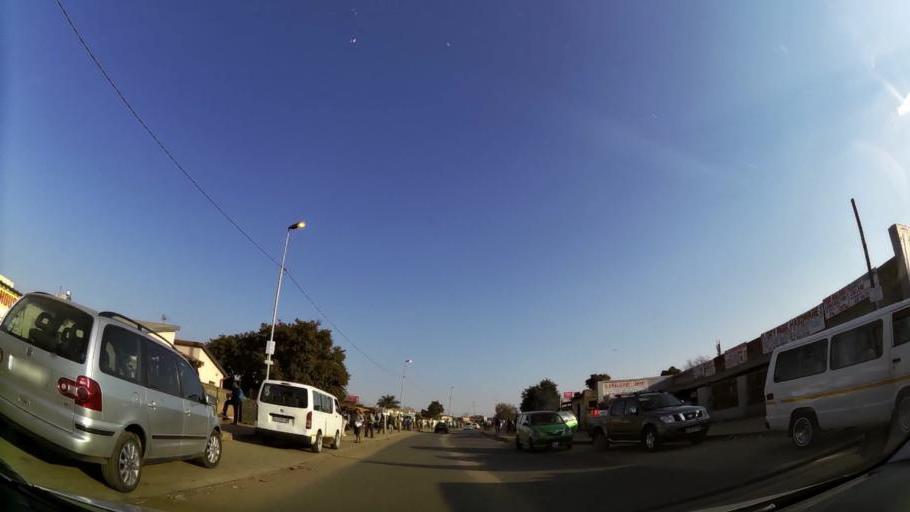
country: ZA
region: Gauteng
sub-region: Ekurhuleni Metropolitan Municipality
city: Tembisa
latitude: -25.9828
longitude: 28.2045
